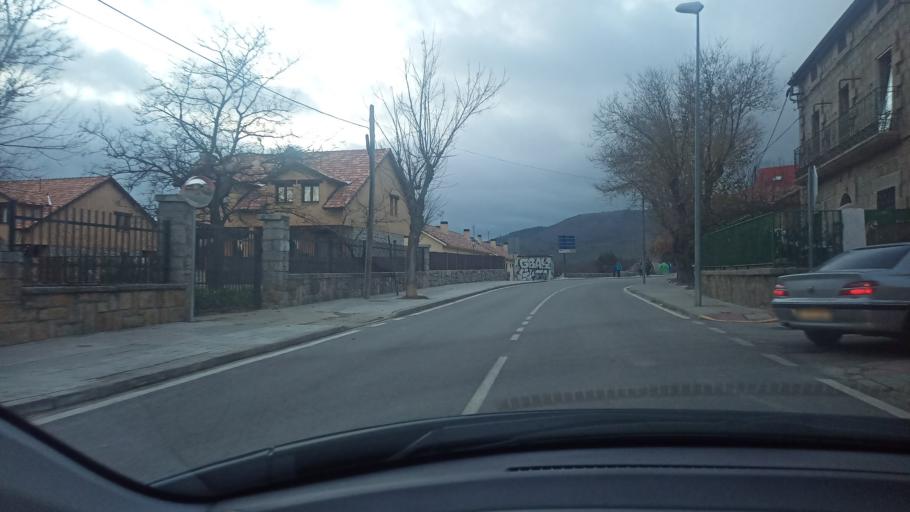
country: ES
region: Madrid
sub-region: Provincia de Madrid
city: Zarzalejo
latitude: 40.5397
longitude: -4.1645
